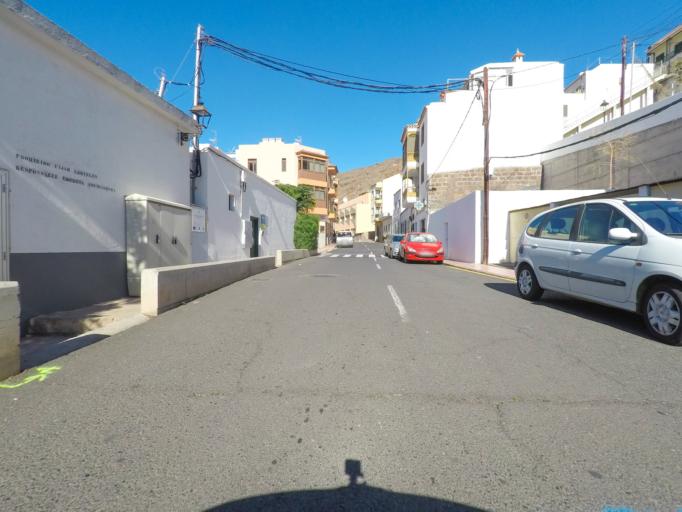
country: ES
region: Canary Islands
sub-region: Provincia de Santa Cruz de Tenerife
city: Alajero
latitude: 28.0303
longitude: -17.1976
